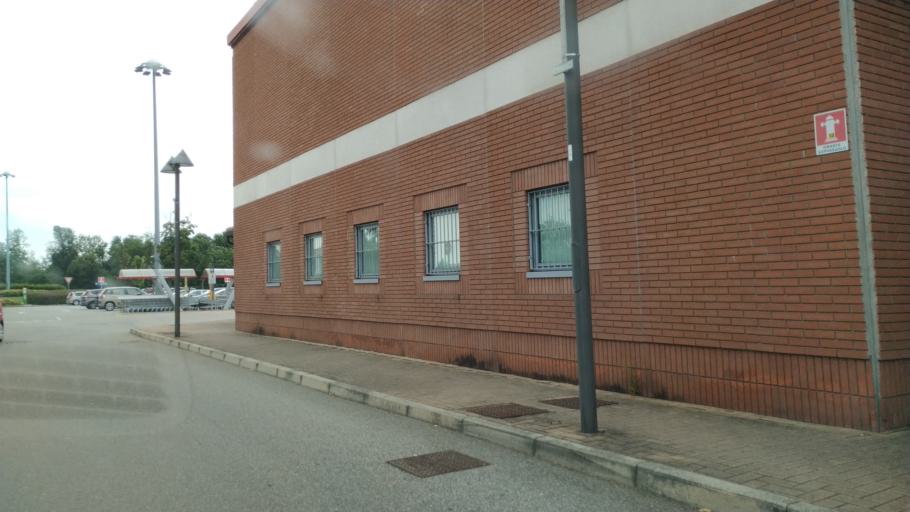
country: IT
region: Piedmont
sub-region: Provincia di Novara
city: Romagnano Sesia
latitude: 45.6230
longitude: 8.4010
